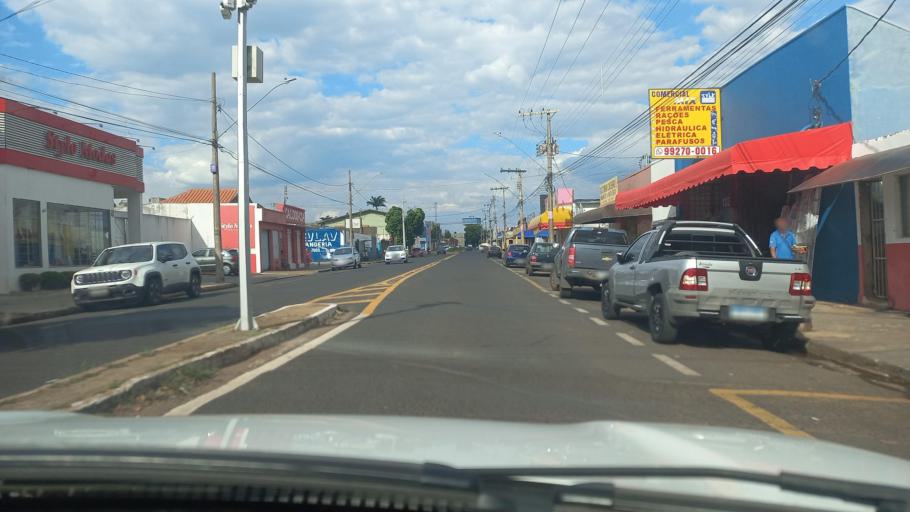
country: BR
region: Minas Gerais
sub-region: Uberaba
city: Uberaba
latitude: -19.7348
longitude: -47.9168
